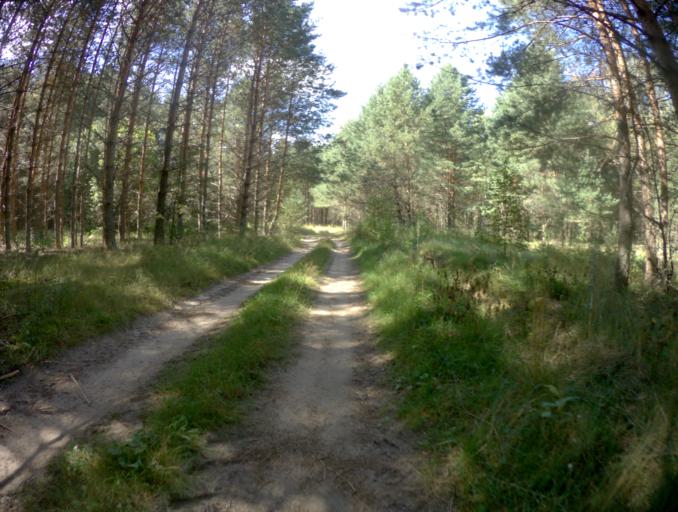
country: RU
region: Vladimir
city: Krasnaya Gorbatka
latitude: 55.9968
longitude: 41.8865
